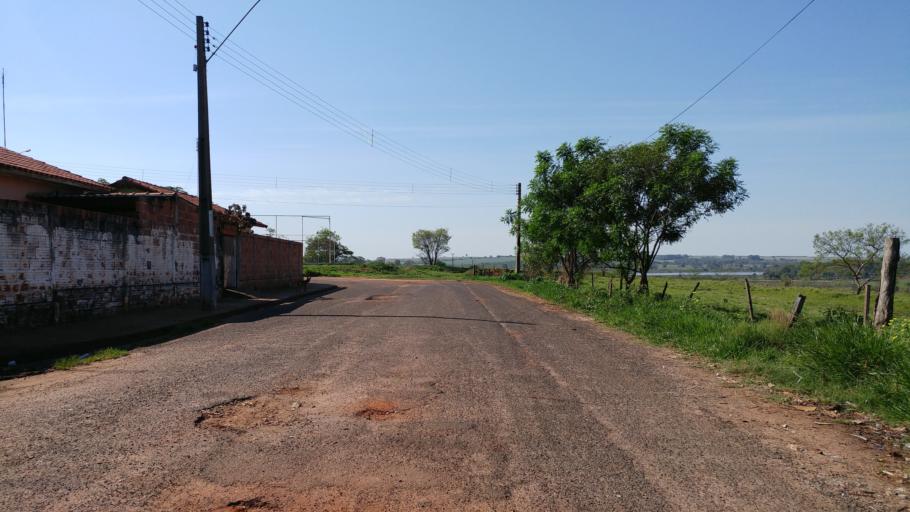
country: BR
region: Sao Paulo
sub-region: Paraguacu Paulista
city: Paraguacu Paulista
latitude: -22.4068
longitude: -50.5630
